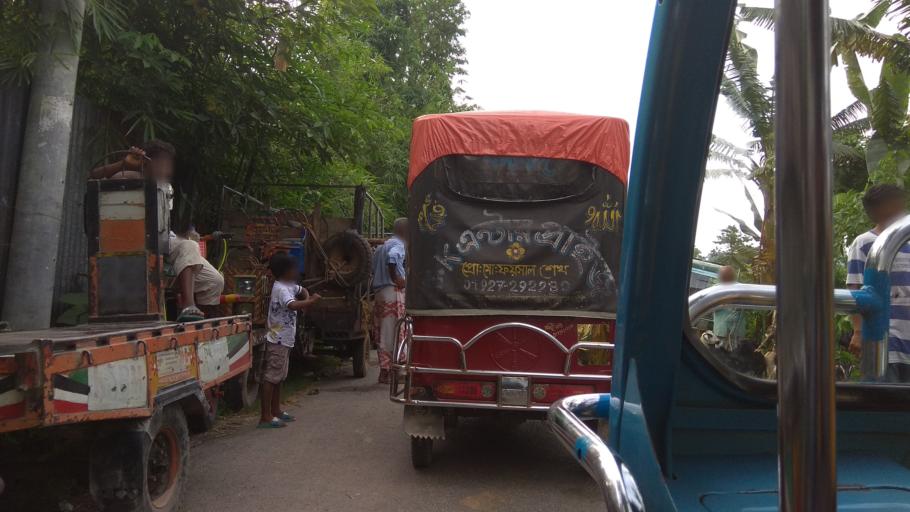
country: BD
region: Khulna
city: Kalia
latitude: 22.9996
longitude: 89.7694
